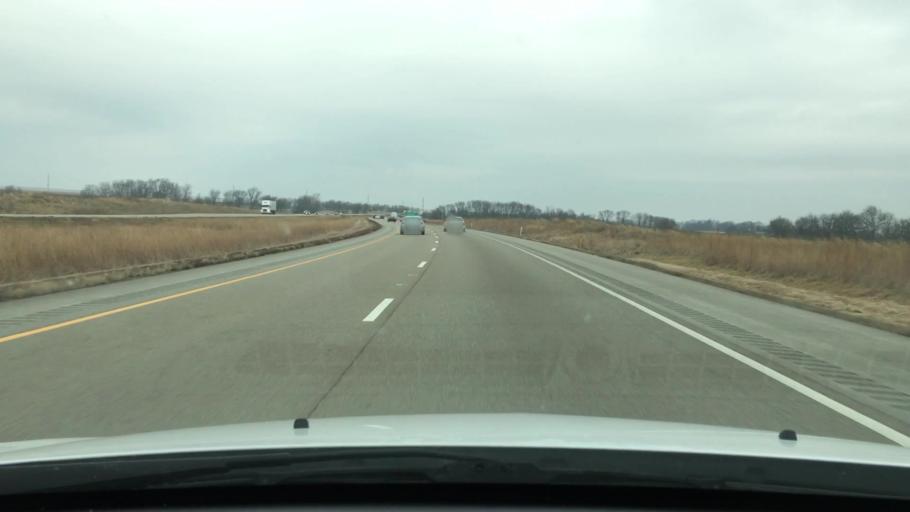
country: US
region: Illinois
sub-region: Logan County
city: Atlanta
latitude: 40.2687
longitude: -89.2130
